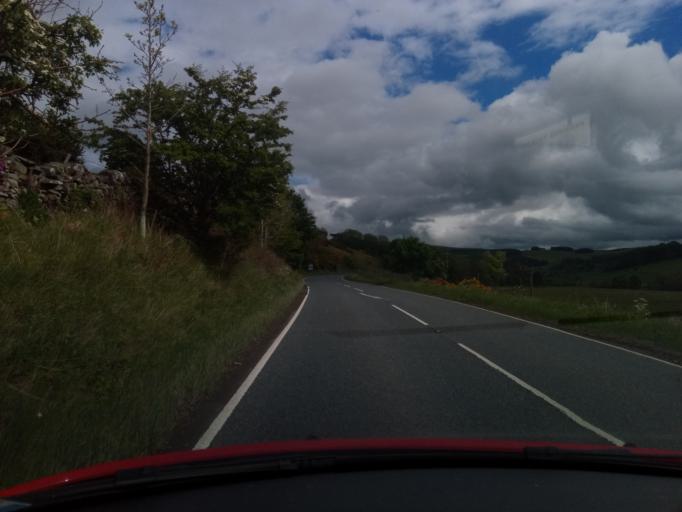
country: GB
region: Scotland
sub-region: The Scottish Borders
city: Galashiels
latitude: 55.7011
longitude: -2.8827
